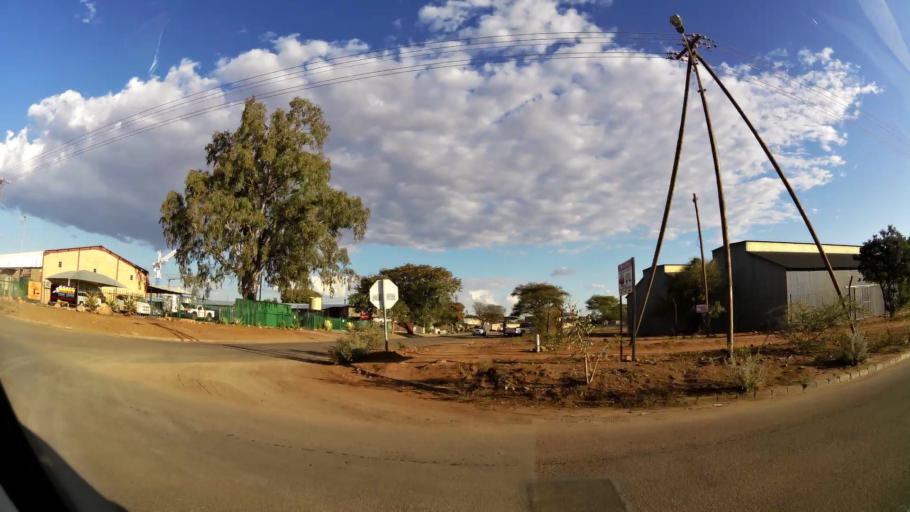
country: ZA
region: Limpopo
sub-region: Waterberg District Municipality
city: Mokopane
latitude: -24.1707
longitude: 29.0024
